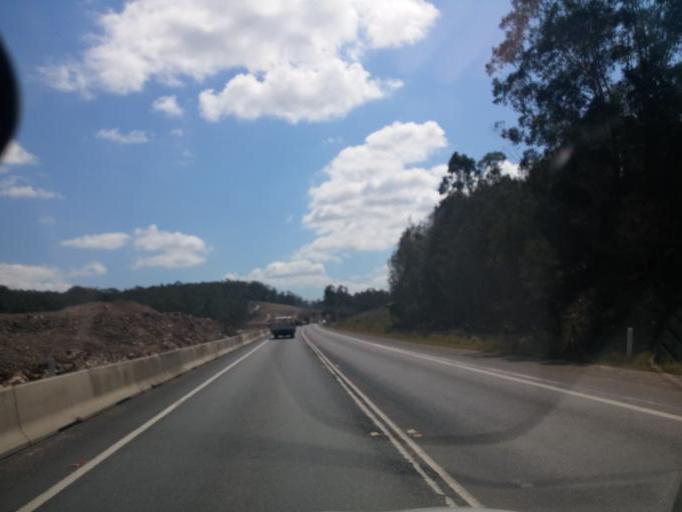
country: AU
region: New South Wales
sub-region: Port Macquarie-Hastings
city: North Shore
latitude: -31.2737
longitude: 152.8124
